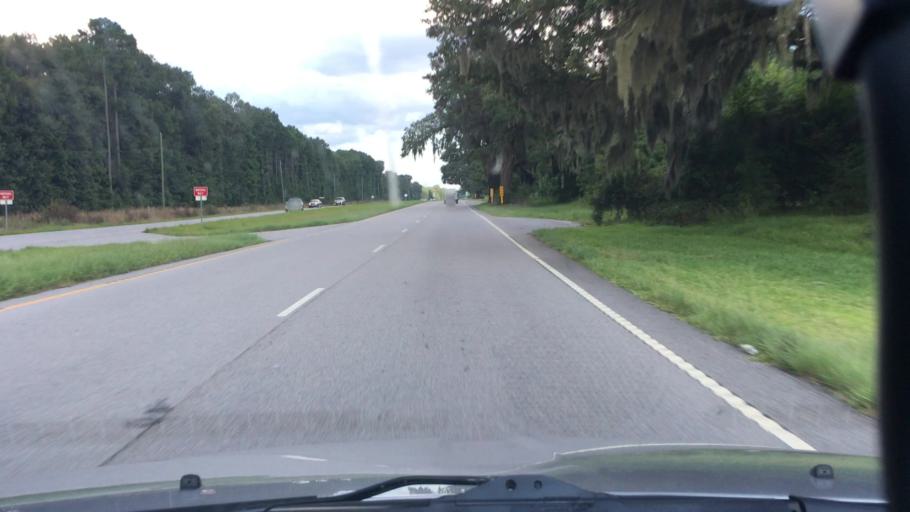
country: US
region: South Carolina
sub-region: Hampton County
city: Yemassee
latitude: 32.6397
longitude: -80.8492
